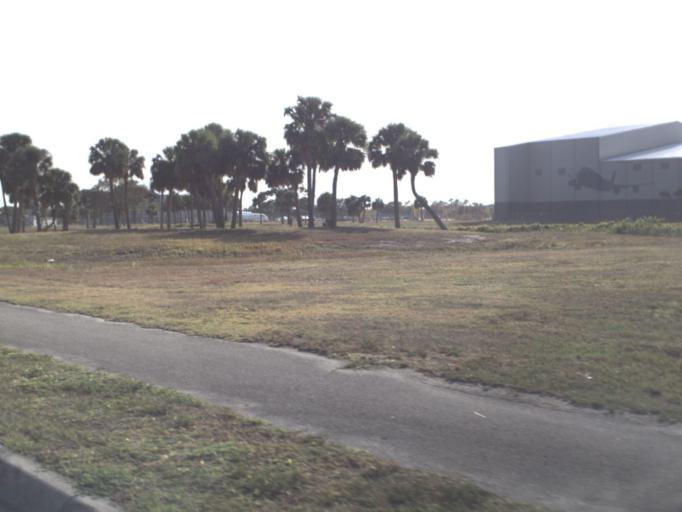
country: US
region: Florida
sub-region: Brevard County
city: Melbourne
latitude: 28.0993
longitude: -80.6233
